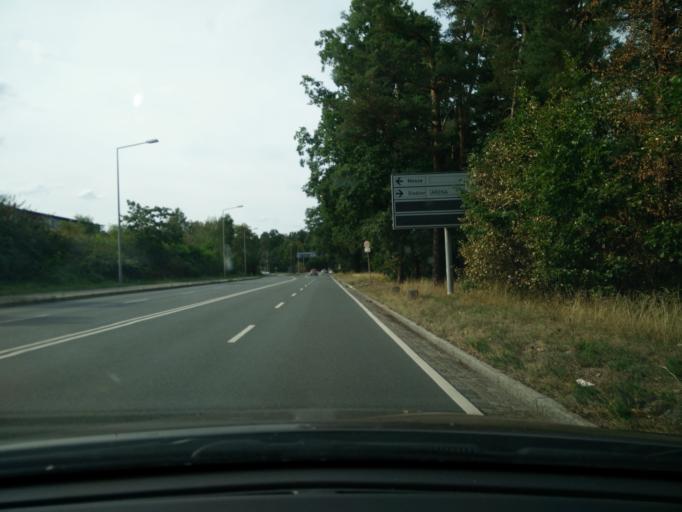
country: DE
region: Bavaria
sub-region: Regierungsbezirk Mittelfranken
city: Nuernberg
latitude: 49.4196
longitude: 11.1339
